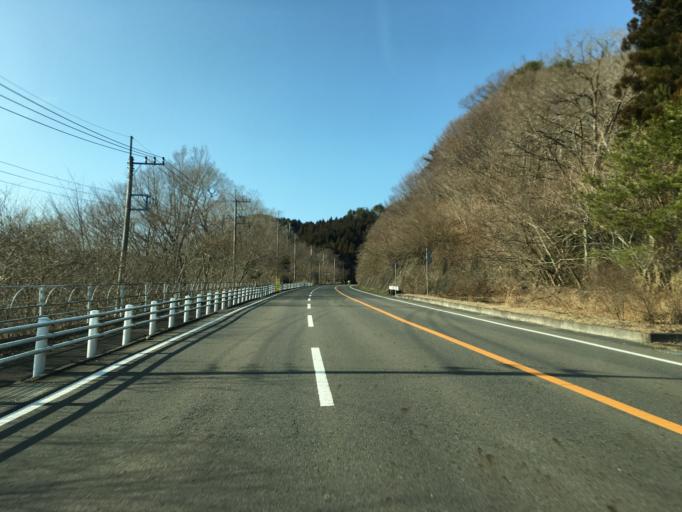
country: JP
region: Ibaraki
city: Takahagi
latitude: 36.7304
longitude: 140.6231
